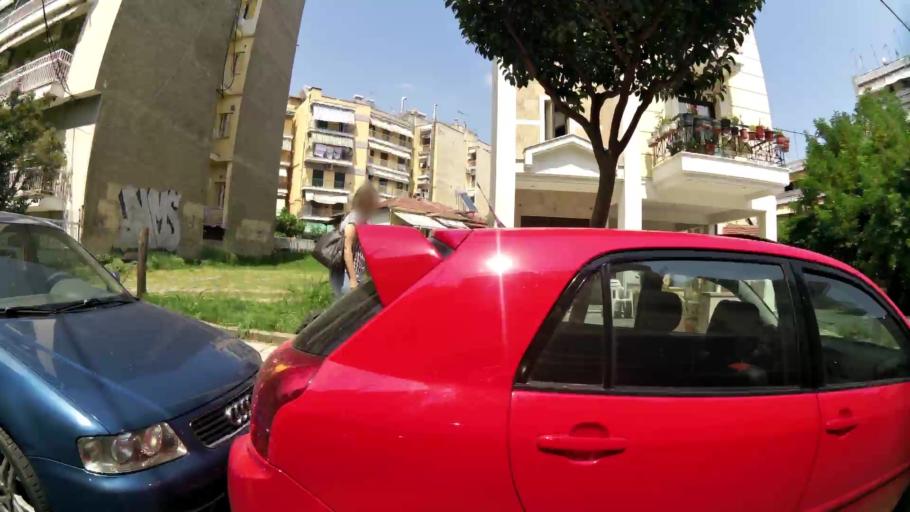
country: GR
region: Central Macedonia
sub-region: Nomos Imathias
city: Veroia
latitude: 40.5228
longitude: 22.2062
